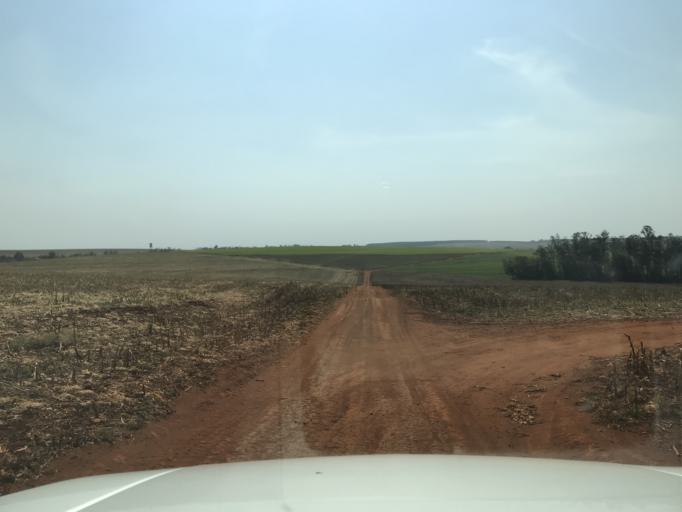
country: BR
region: Parana
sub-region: Palotina
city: Palotina
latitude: -24.2332
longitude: -53.7472
